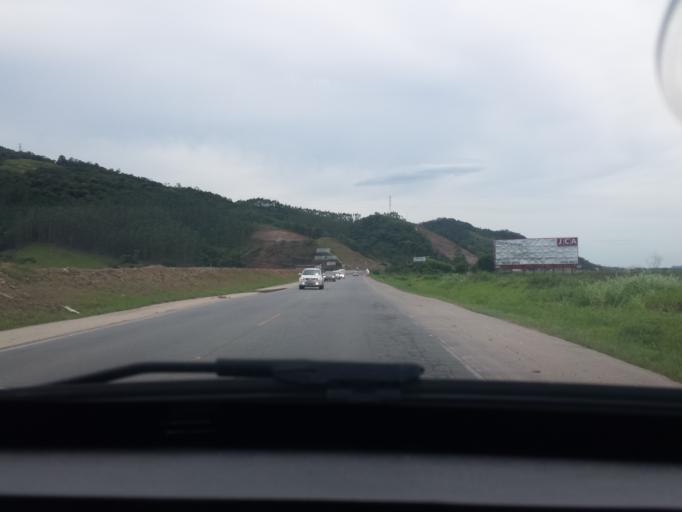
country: BR
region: Santa Catarina
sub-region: Gaspar
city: Gaspar
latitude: -26.8961
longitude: -48.9207
